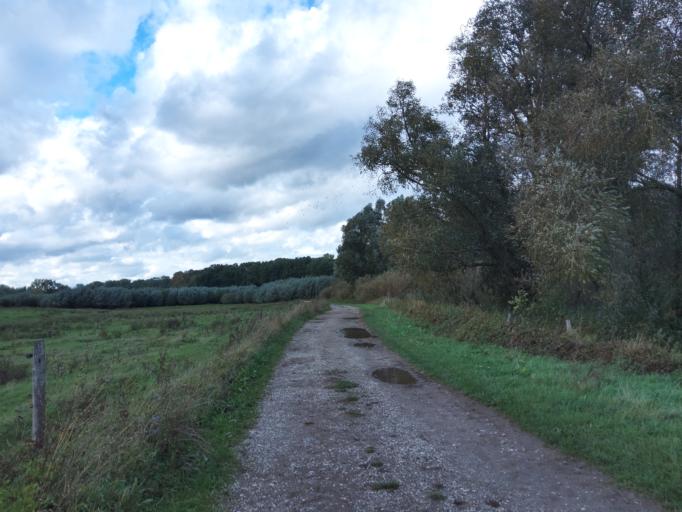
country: NL
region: Gelderland
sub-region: Gemeente Neerijnen
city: Neerijnen
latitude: 51.8275
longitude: 5.2809
